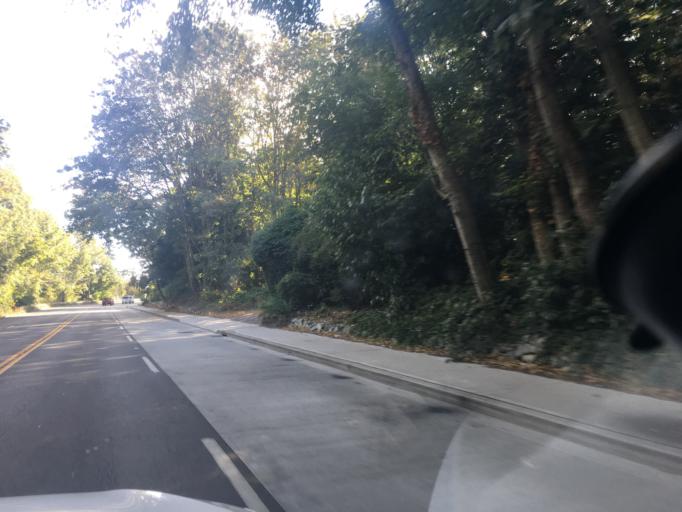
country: US
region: Washington
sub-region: King County
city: Shoreline
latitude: 47.7064
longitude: -122.3368
